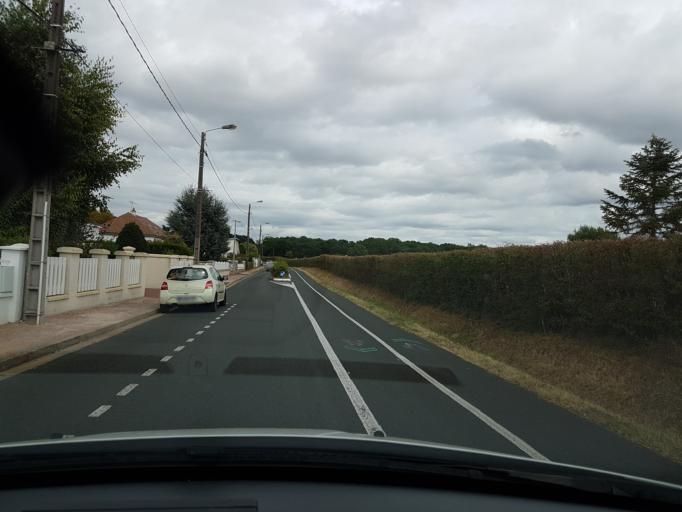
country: FR
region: Centre
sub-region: Departement d'Indre-et-Loire
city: Chambray-les-Tours
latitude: 47.3320
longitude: 0.7108
